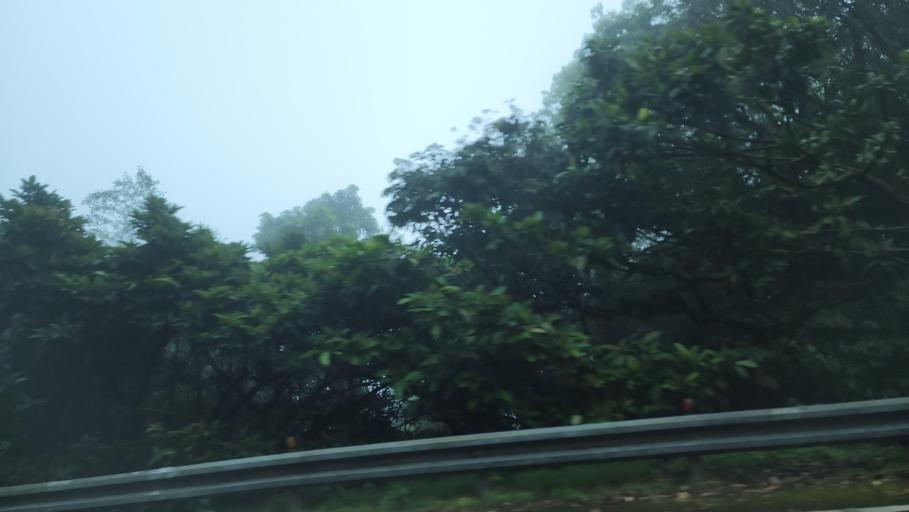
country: TW
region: Taipei
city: Taipei
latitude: 25.1434
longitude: 121.6027
